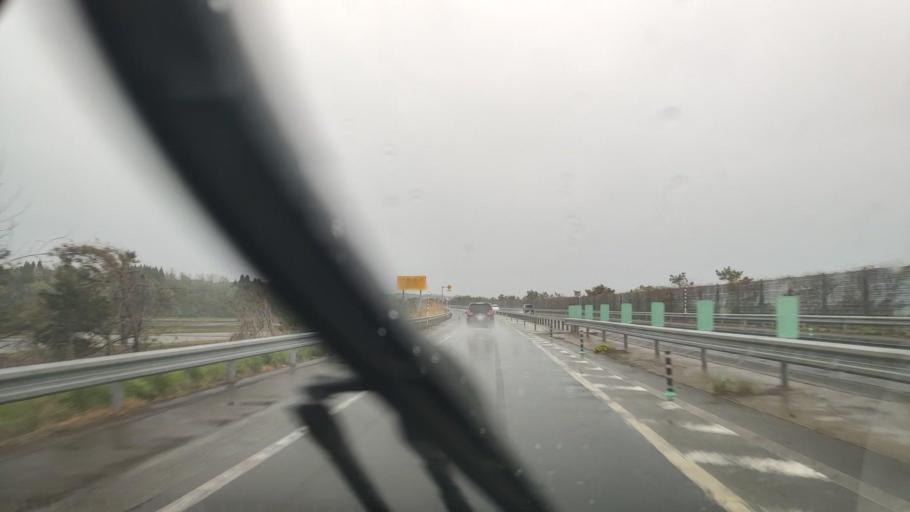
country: JP
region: Akita
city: Noshiromachi
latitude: 40.1816
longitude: 140.0660
